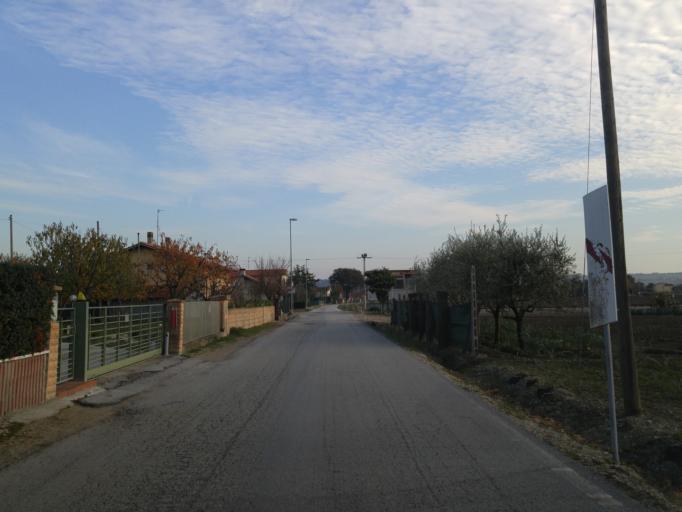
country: IT
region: The Marches
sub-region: Provincia di Pesaro e Urbino
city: Cuccurano
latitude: 43.7918
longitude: 12.9569
